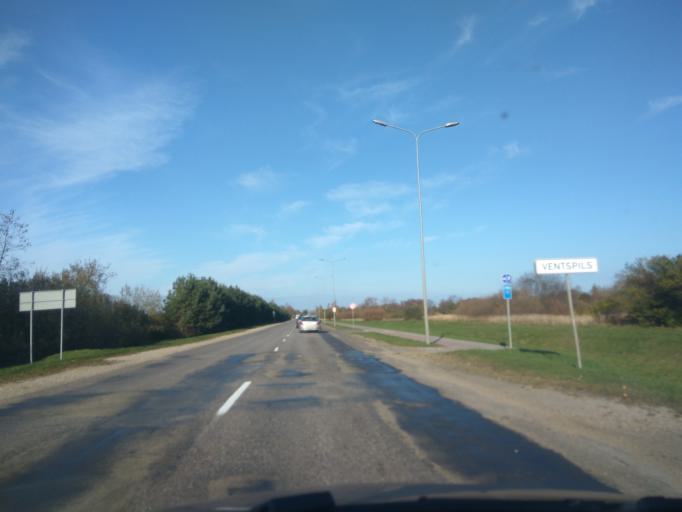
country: LV
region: Ventspils
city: Ventspils
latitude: 57.3542
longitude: 21.5641
